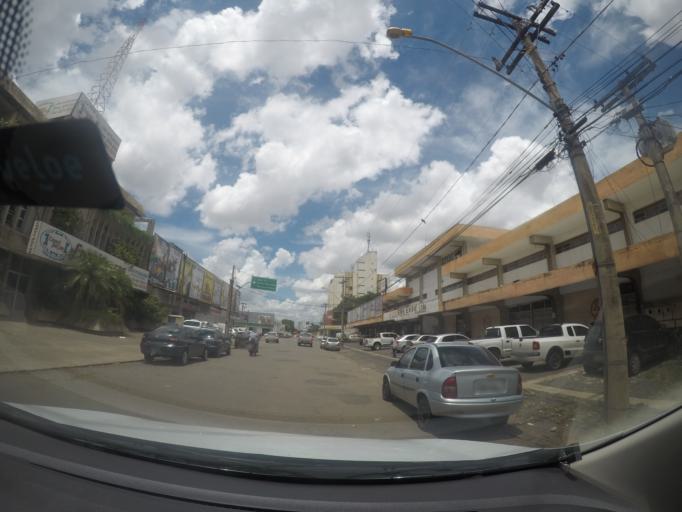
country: BR
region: Goias
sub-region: Goiania
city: Goiania
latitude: -16.6721
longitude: -49.3064
